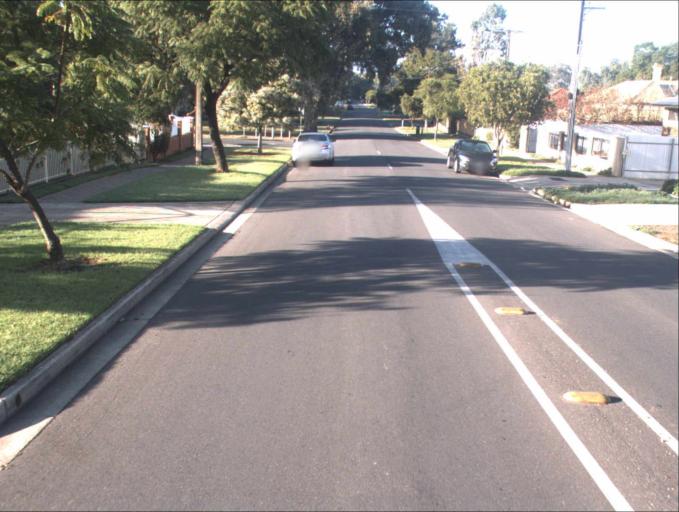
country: AU
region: South Australia
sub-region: Port Adelaide Enfield
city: Klemzig
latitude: -34.8756
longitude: 138.6459
